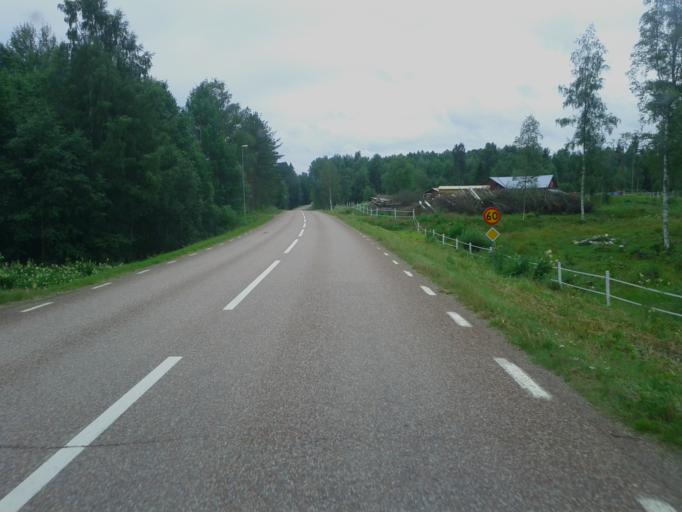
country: SE
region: Dalarna
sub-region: Borlange Kommun
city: Borlaenge
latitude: 60.3402
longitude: 15.4034
